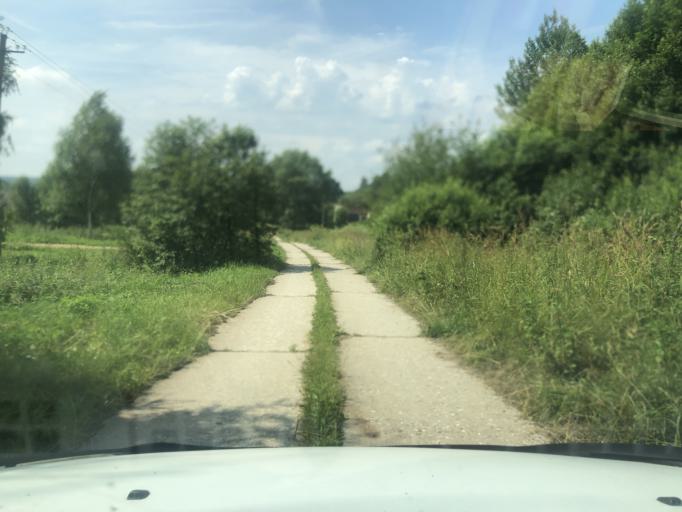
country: RU
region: Jaroslavl
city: Pereslavl'-Zalesskiy
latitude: 57.0458
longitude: 38.8704
